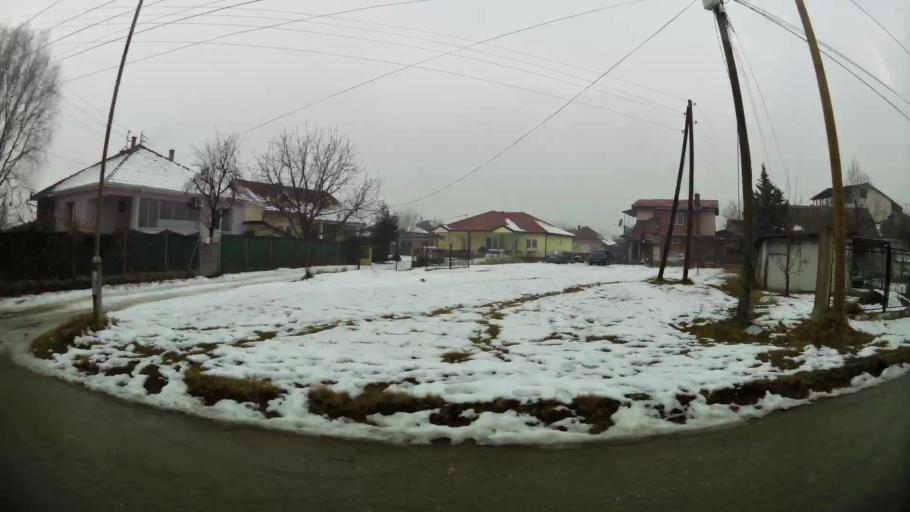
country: MK
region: Petrovec
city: Petrovec
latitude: 41.9366
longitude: 21.6172
